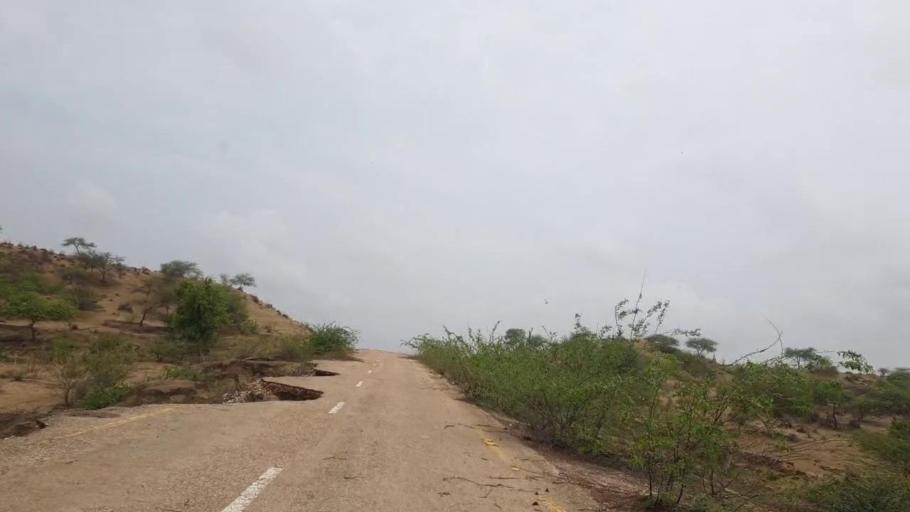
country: PK
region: Sindh
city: Naukot
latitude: 24.6310
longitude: 69.3549
